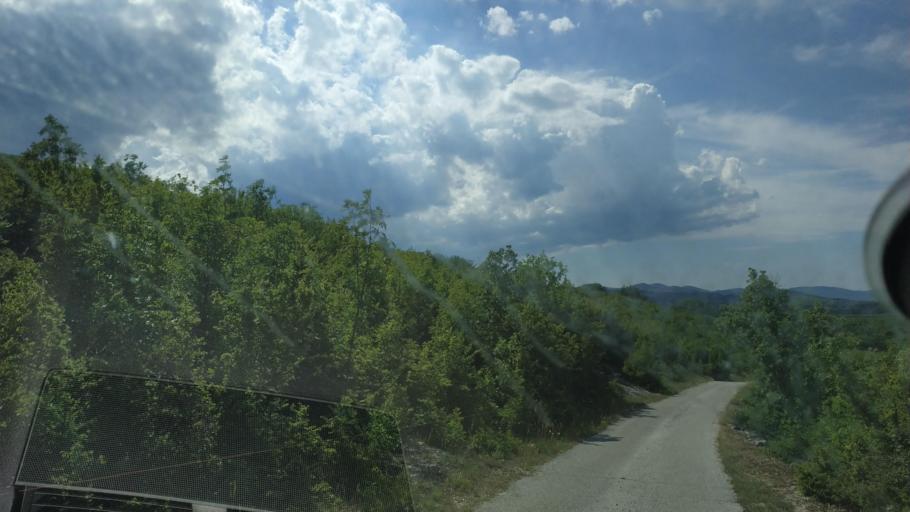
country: HR
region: Splitsko-Dalmatinska
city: Greda
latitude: 43.5847
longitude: 16.6563
